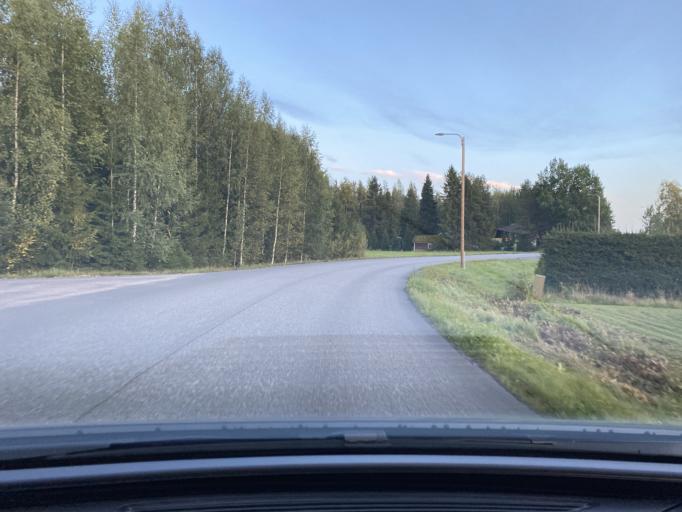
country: FI
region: Satakunta
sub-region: Pori
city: Huittinen
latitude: 61.1722
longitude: 22.7141
